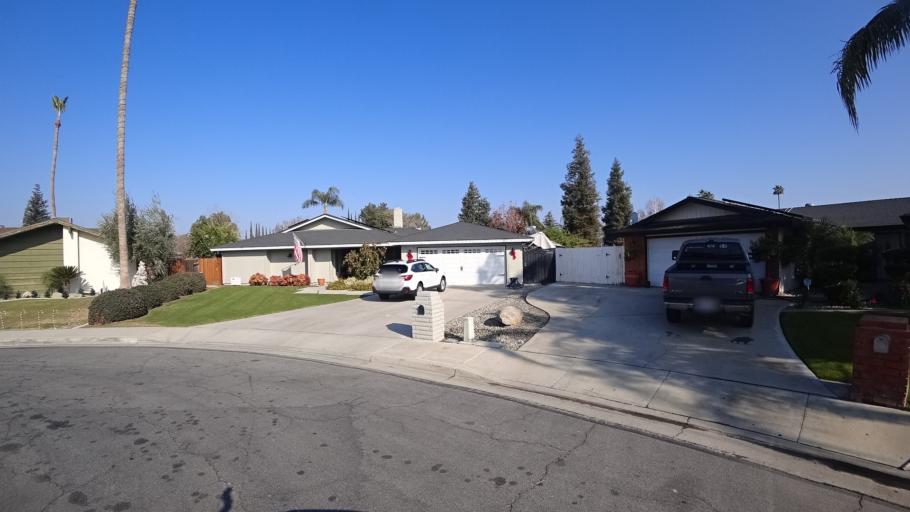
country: US
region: California
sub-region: Kern County
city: Greenacres
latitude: 35.3586
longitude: -119.0767
